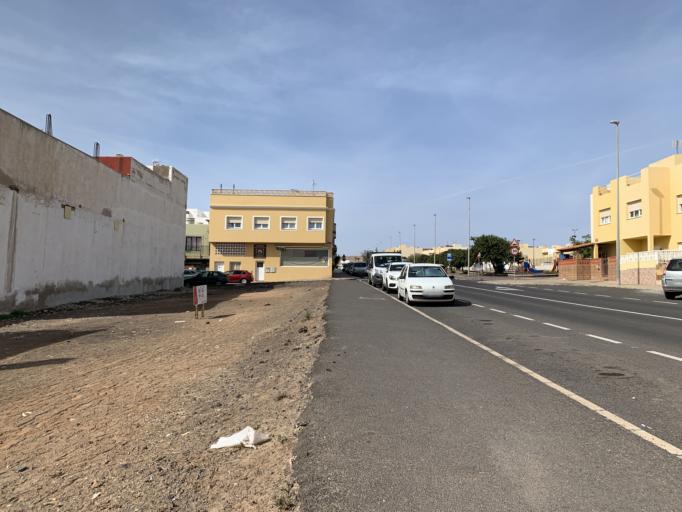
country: ES
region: Canary Islands
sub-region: Provincia de Las Palmas
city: Puerto del Rosario
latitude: 28.5099
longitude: -13.8603
